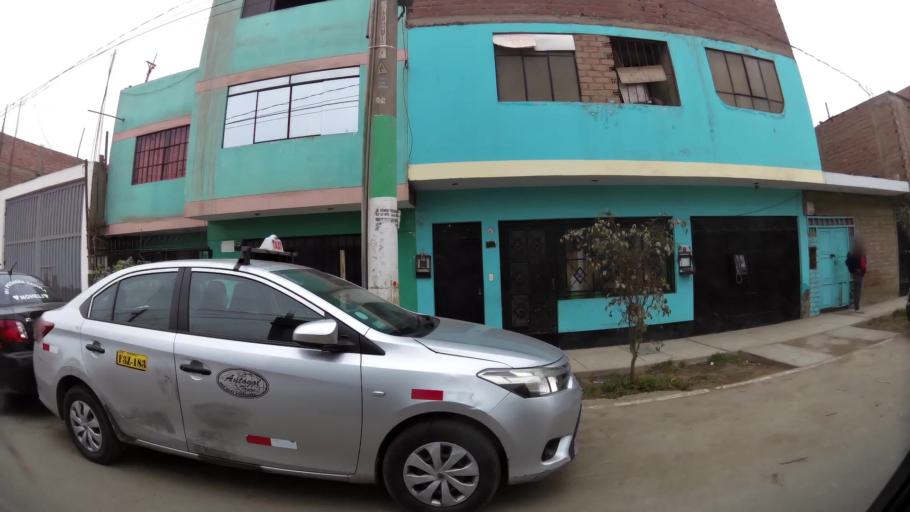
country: PE
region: Lima
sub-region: Lima
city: Urb. Santo Domingo
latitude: -11.8878
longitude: -77.0668
